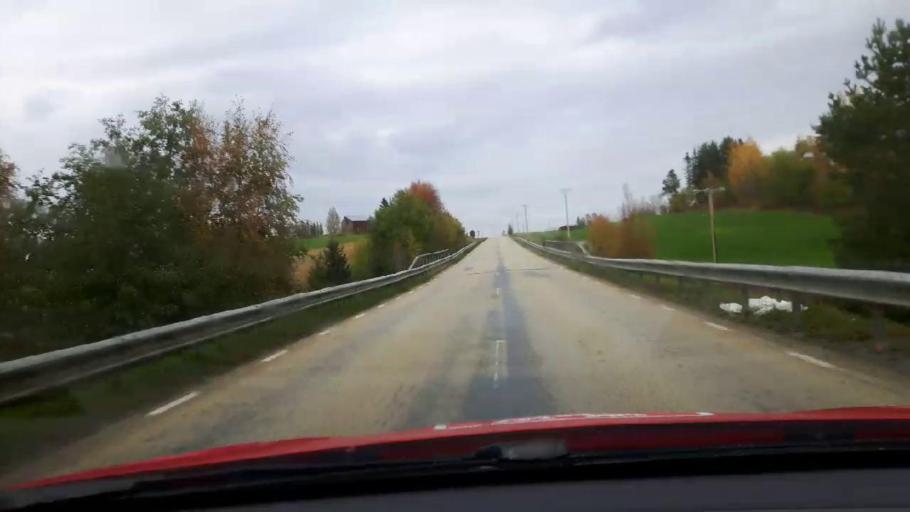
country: SE
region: Jaemtland
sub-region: Bergs Kommun
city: Hoverberg
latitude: 62.9560
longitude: 14.3420
